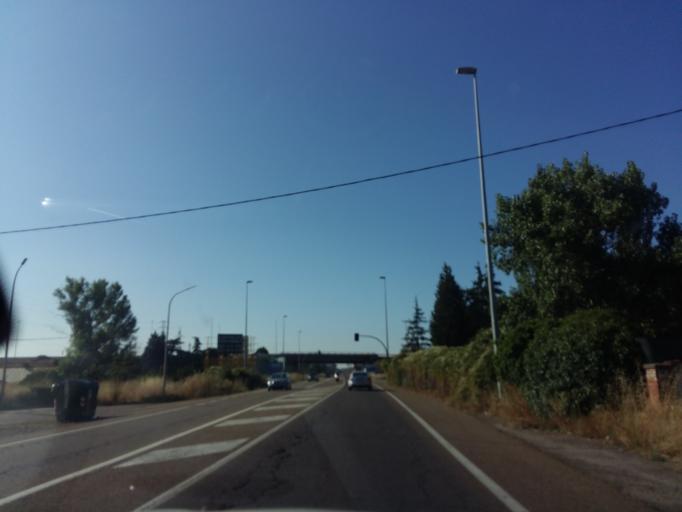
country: ES
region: Castille and Leon
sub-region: Provincia de Leon
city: Leon
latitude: 42.5712
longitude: -5.5828
